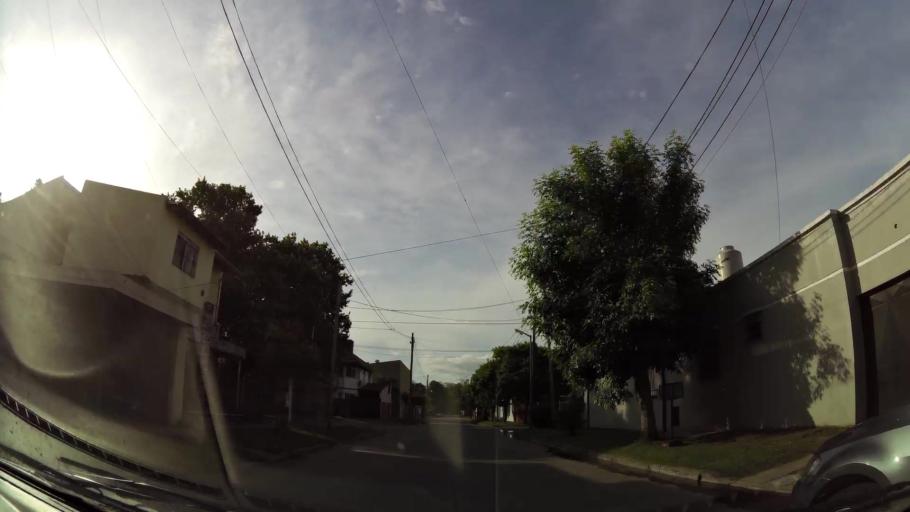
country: AR
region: Buenos Aires
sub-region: Partido de Quilmes
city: Quilmes
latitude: -34.7381
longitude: -58.2561
